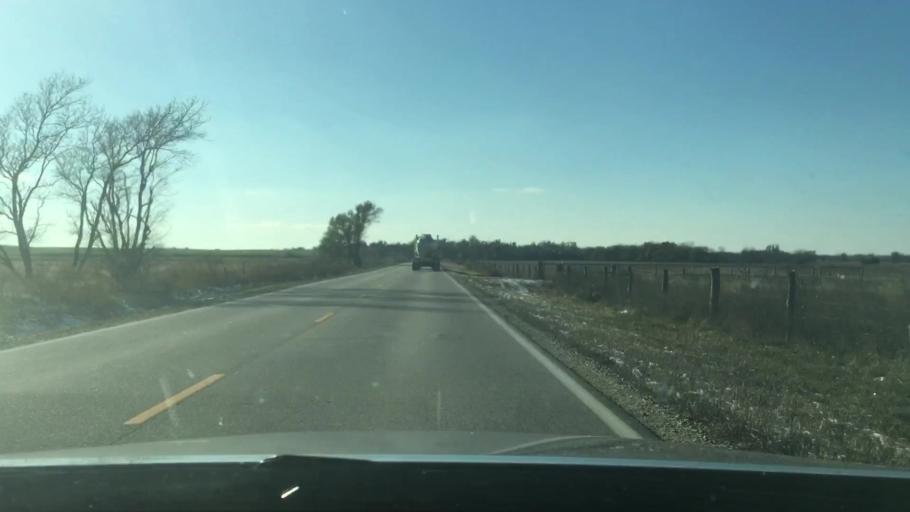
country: US
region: Kansas
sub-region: Reno County
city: Nickerson
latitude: 38.1449
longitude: -98.1288
